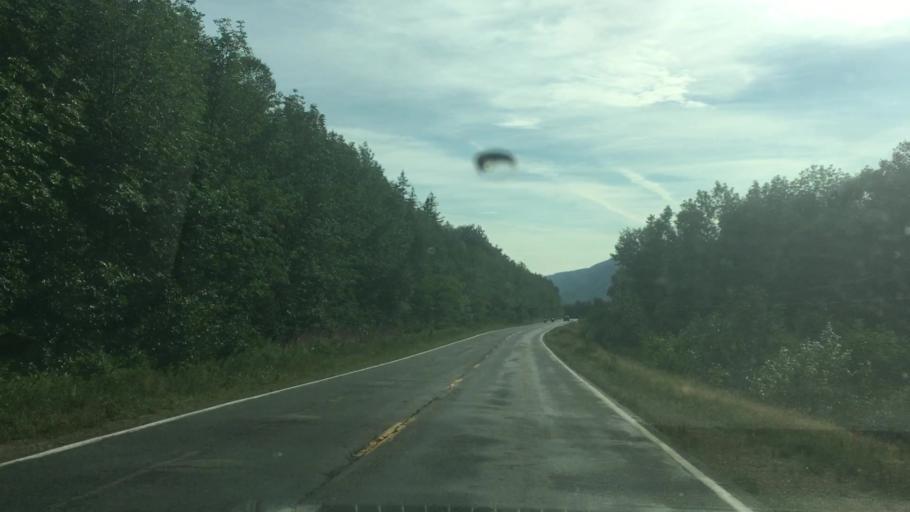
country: CA
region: Nova Scotia
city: Sydney Mines
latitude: 46.8620
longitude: -60.5656
